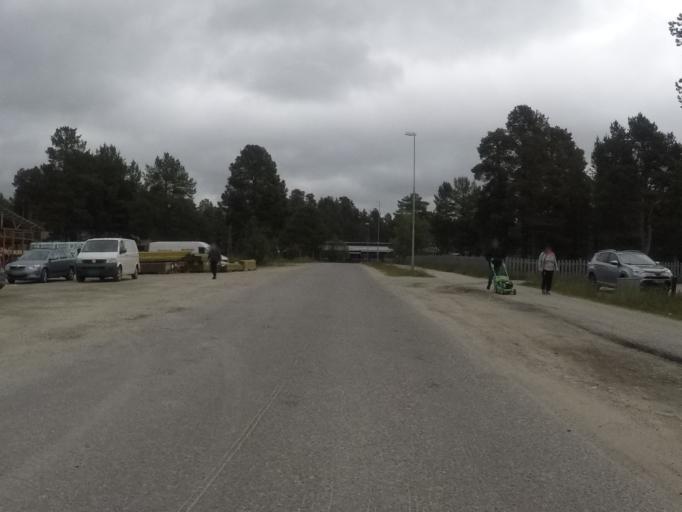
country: NO
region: Finnmark Fylke
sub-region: Karasjok
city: Karasjohka
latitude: 69.4721
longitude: 25.5233
